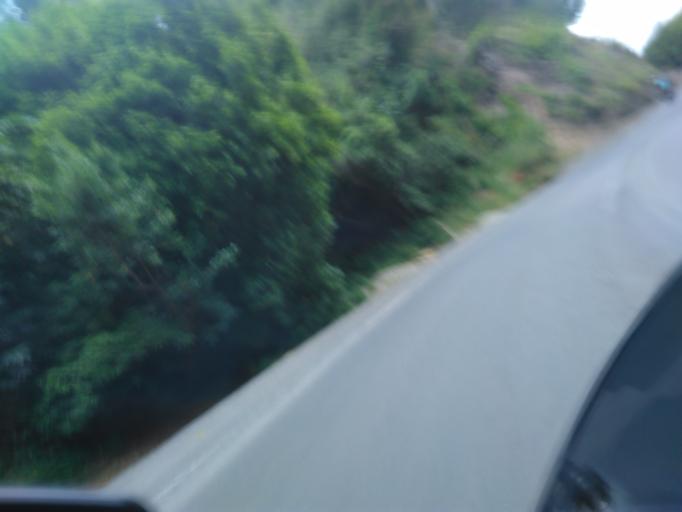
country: NZ
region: Bay of Plenty
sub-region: Opotiki District
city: Opotiki
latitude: -38.3455
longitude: 177.4492
